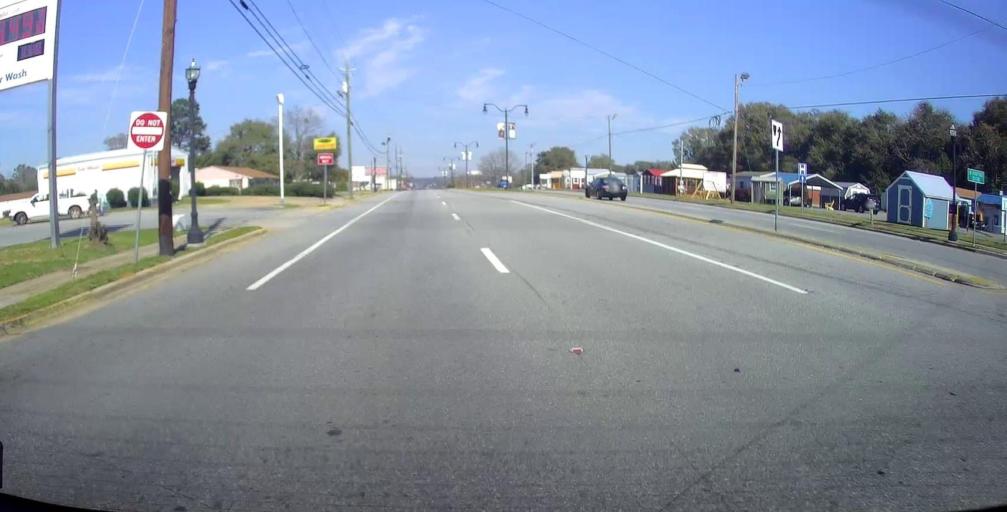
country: US
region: Georgia
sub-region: Houston County
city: Perry
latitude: 32.4468
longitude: -83.7500
